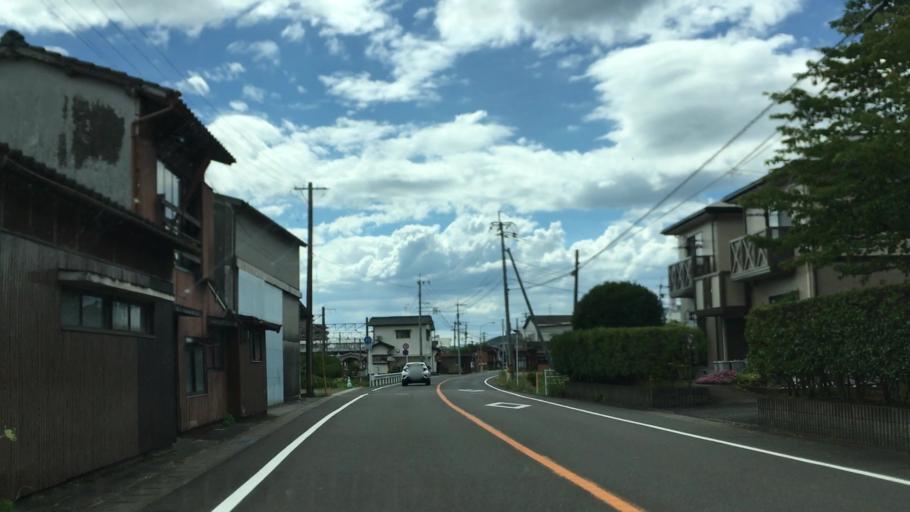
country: JP
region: Saga Prefecture
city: Kashima
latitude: 33.2195
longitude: 130.1642
